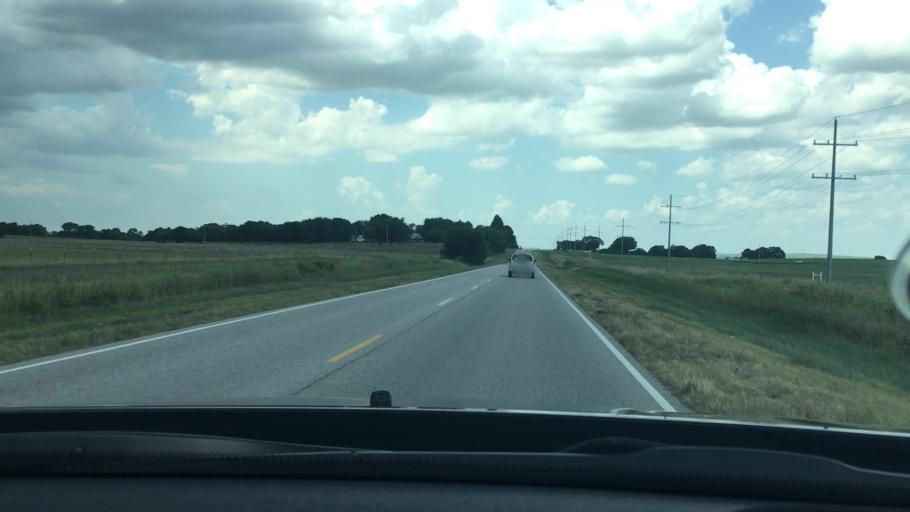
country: US
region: Oklahoma
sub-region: Pontotoc County
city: Ada
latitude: 34.6673
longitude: -96.6349
